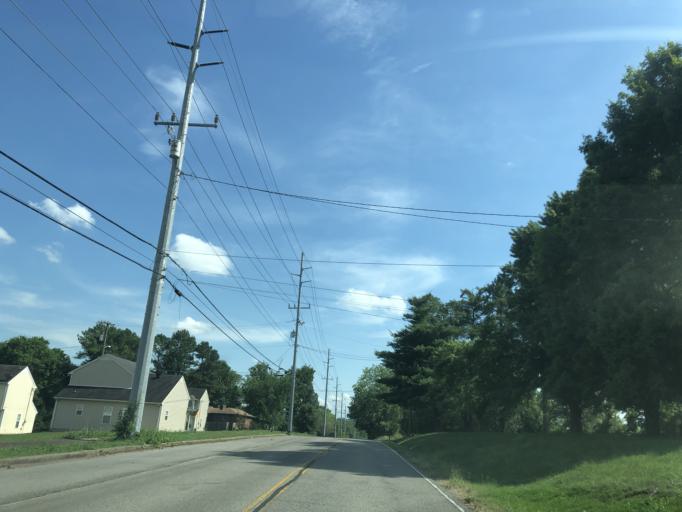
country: US
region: Tennessee
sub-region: Davidson County
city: Nashville
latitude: 36.2417
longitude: -86.8022
